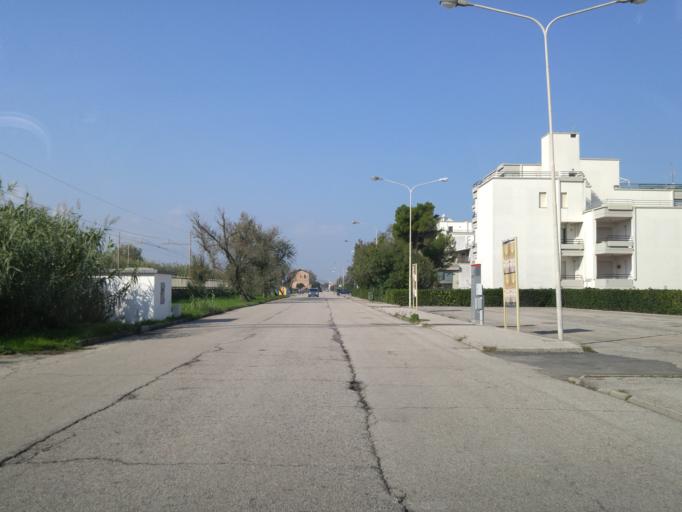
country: IT
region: The Marches
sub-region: Provincia di Pesaro e Urbino
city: Fano
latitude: 43.8339
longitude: 13.0443
